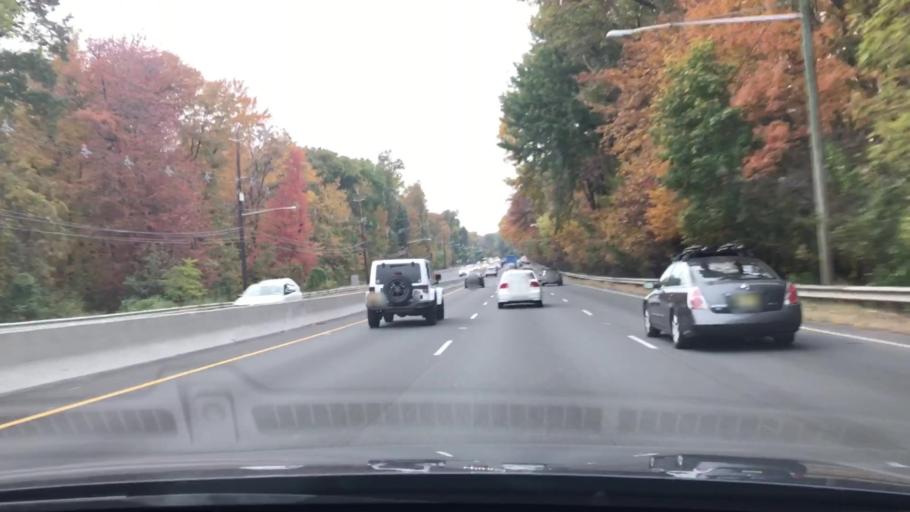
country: US
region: New Jersey
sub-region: Bergen County
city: Englewood
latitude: 40.8843
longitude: -73.9897
